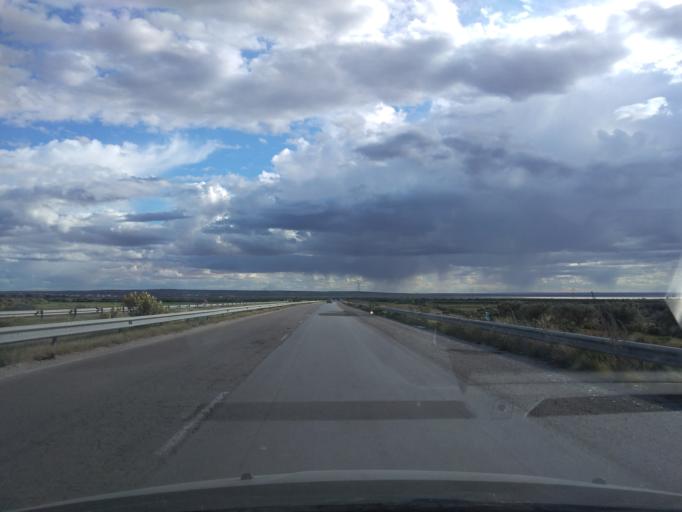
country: TN
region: Al Munastir
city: Manzil Kamil
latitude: 35.5153
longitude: 10.6264
